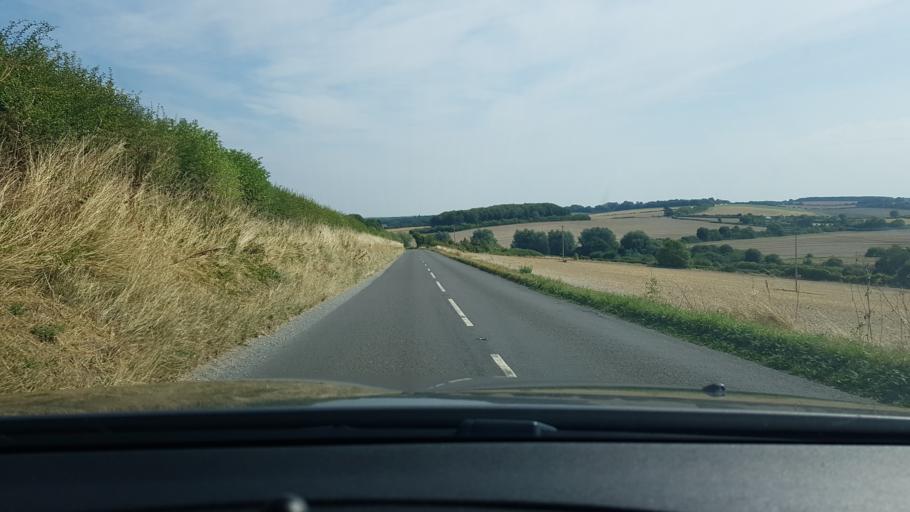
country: GB
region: England
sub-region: Wiltshire
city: Shalbourne
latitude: 51.3715
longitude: -1.5516
